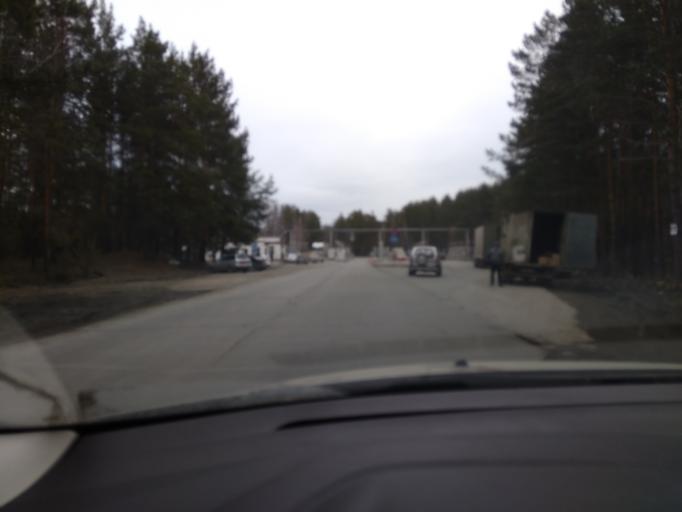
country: RU
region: Chelyabinsk
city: Kyshtym
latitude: 55.7169
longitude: 60.6232
